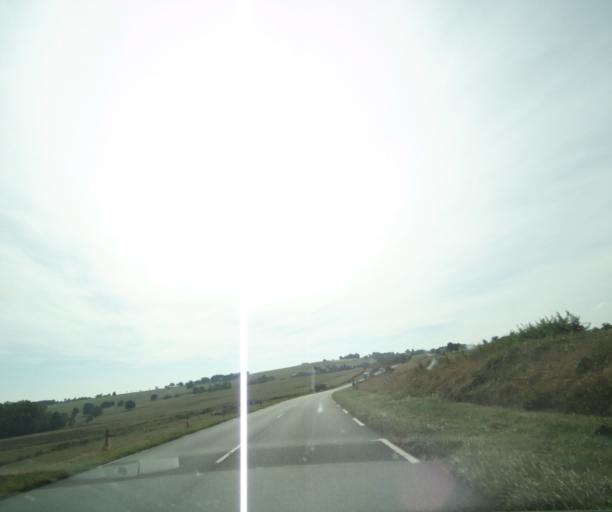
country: FR
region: Auvergne
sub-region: Departement de l'Allier
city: Le Donjon
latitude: 46.3196
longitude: 3.7691
